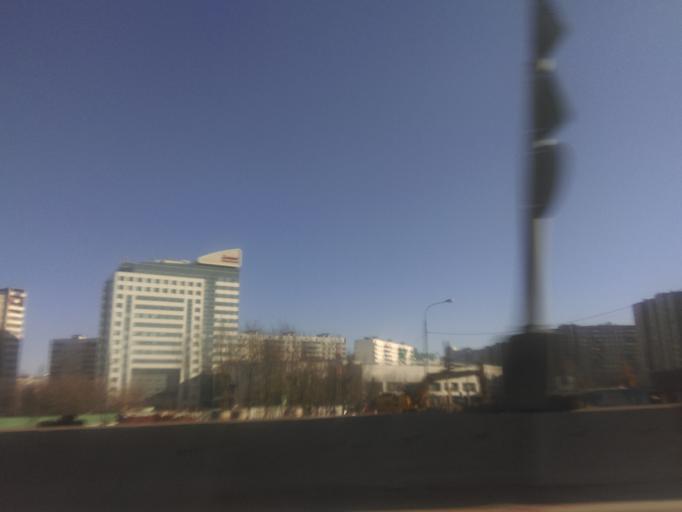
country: RU
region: Moskovskaya
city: Mosrentgen
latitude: 55.6289
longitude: 37.4712
